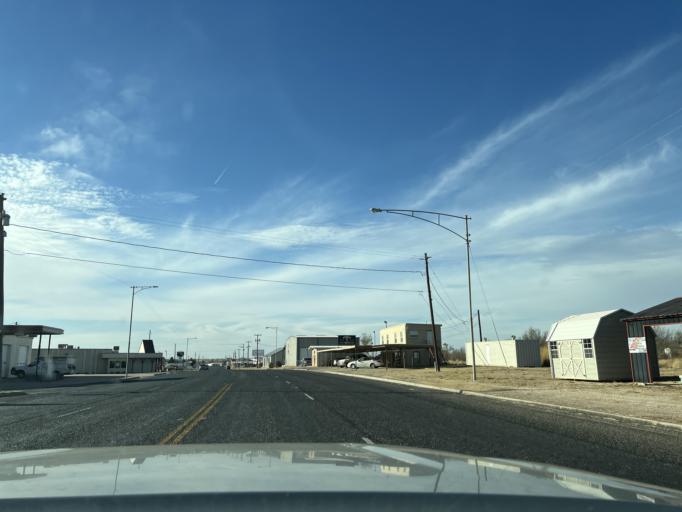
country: US
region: Texas
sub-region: Scurry County
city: Snyder
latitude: 32.7144
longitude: -100.8971
